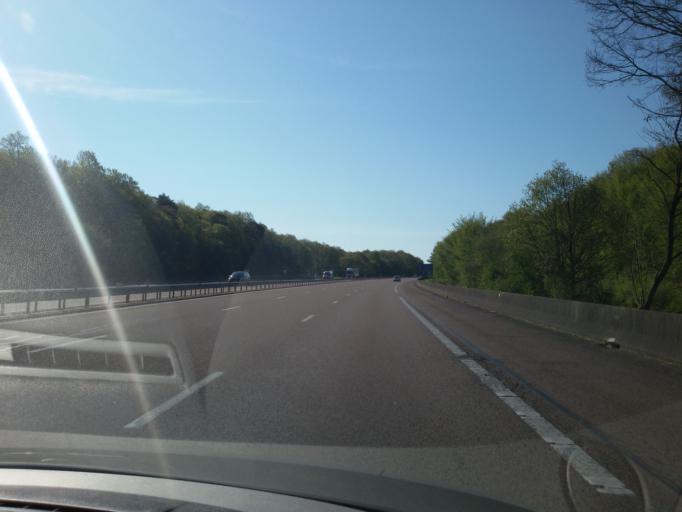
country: FR
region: Bourgogne
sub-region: Departement de l'Yonne
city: Aillant-sur-Tholon
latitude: 47.9215
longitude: 3.2837
